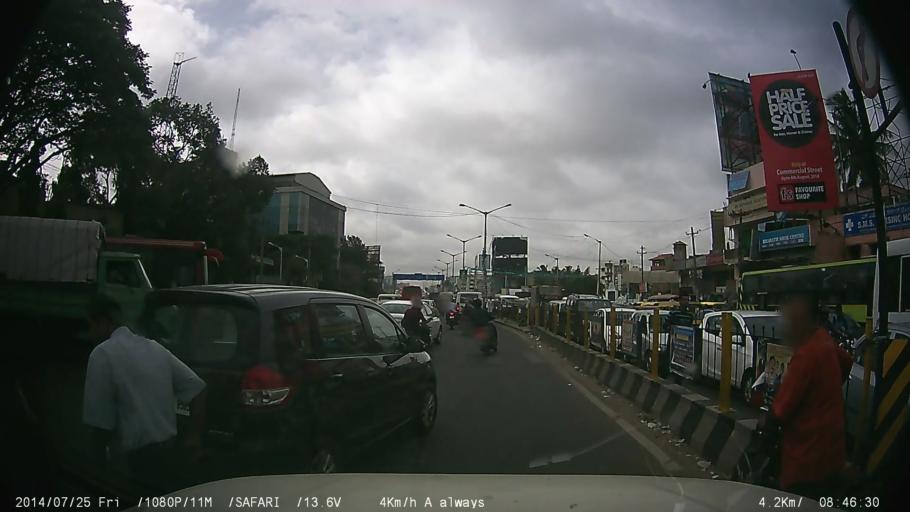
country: IN
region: Karnataka
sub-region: Bangalore Urban
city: Bangalore
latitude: 12.9209
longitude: 77.6204
